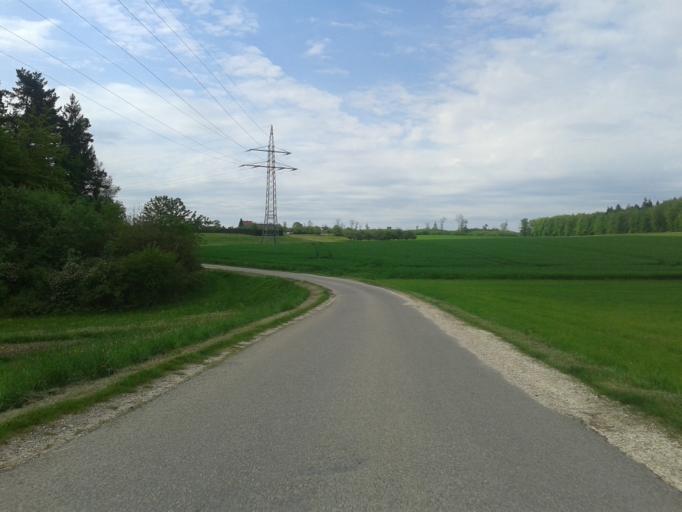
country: DE
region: Baden-Wuerttemberg
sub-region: Tuebingen Region
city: Blaubeuren
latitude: 48.3887
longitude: 9.7879
